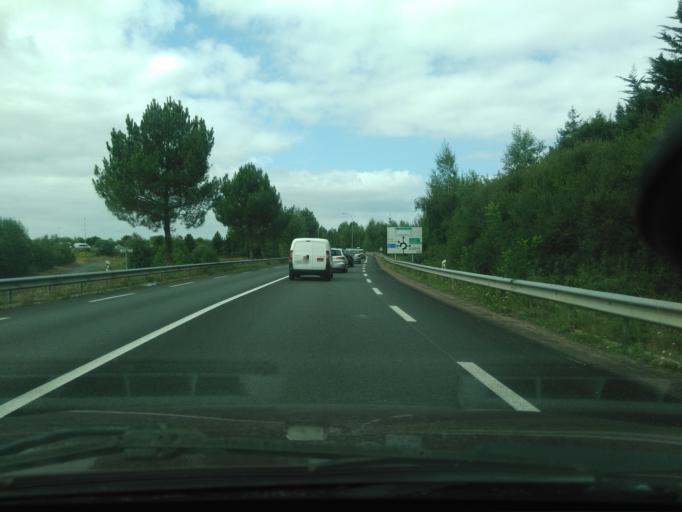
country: FR
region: Pays de la Loire
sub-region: Departement de la Vendee
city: La Roche-sur-Yon
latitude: 46.6795
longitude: -1.3962
